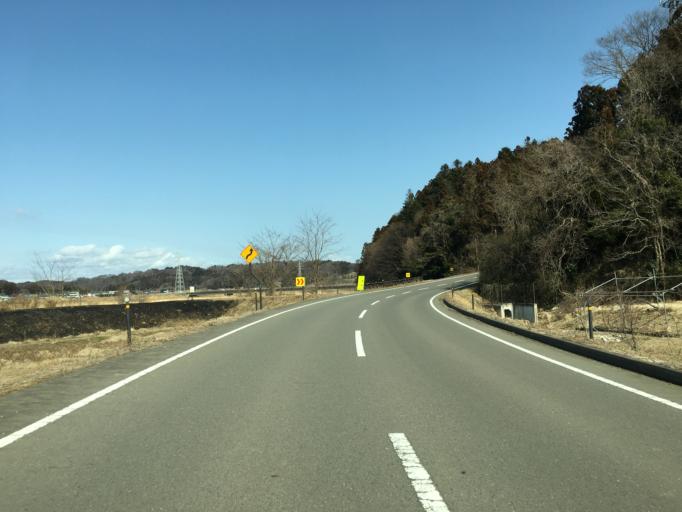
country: JP
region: Fukushima
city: Ishikawa
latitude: 37.1222
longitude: 140.2755
